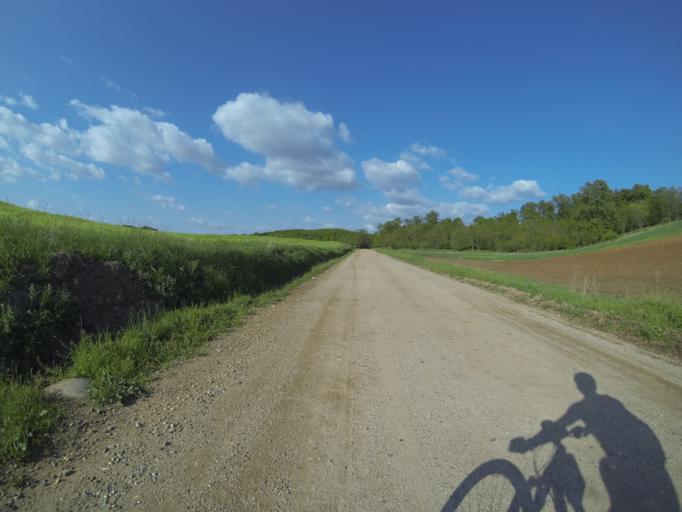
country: RO
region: Dolj
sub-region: Comuna Verbita
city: Verbita
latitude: 44.2875
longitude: 23.2001
